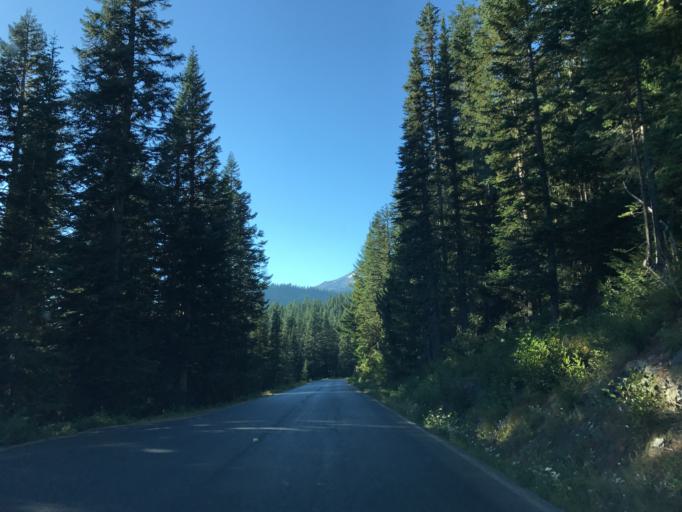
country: US
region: Washington
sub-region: Pierce County
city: Buckley
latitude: 46.7744
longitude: -121.7518
